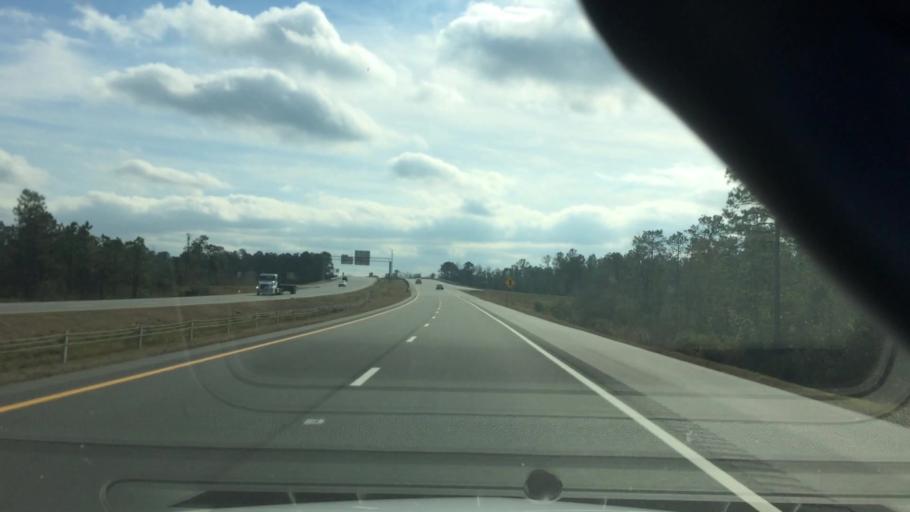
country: US
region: North Carolina
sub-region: Brunswick County
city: Leland
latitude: 34.2619
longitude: -78.0799
